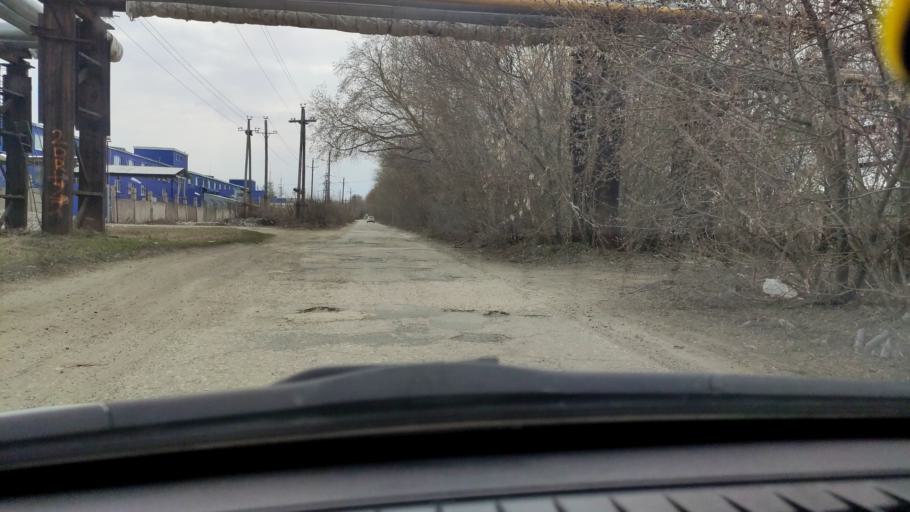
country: RU
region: Samara
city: Tol'yatti
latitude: 53.5239
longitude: 49.4561
